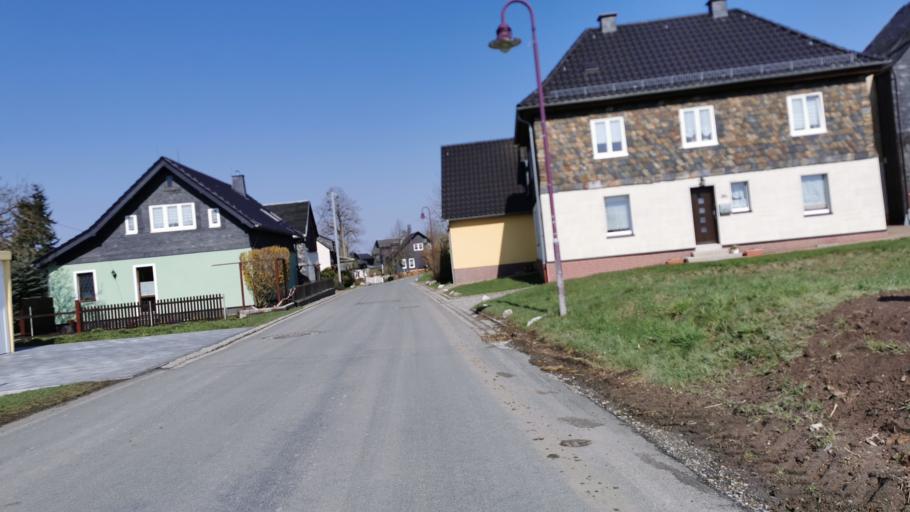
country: DE
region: Thuringia
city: Leutenberg
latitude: 50.5364
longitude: 11.4258
